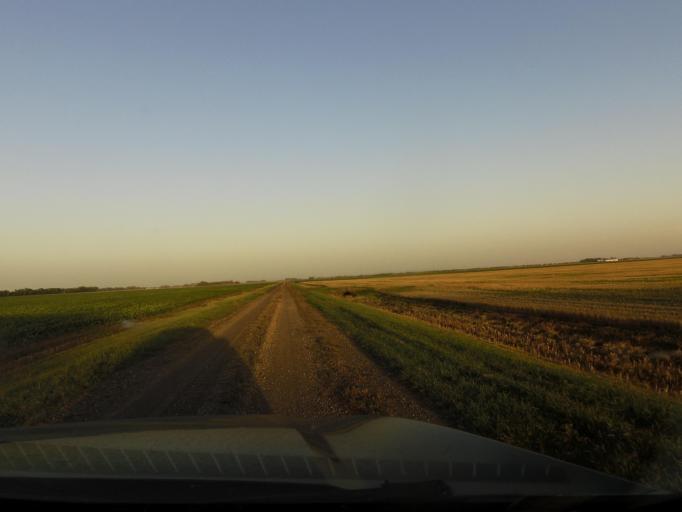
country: US
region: North Dakota
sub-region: Walsh County
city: Grafton
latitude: 48.3831
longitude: -97.2513
